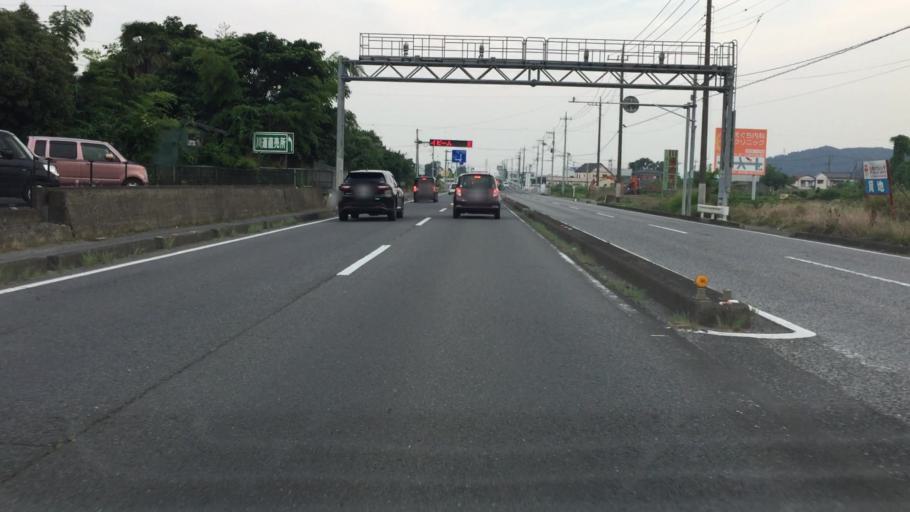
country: JP
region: Tochigi
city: Tochigi
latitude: 36.3582
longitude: 139.7157
